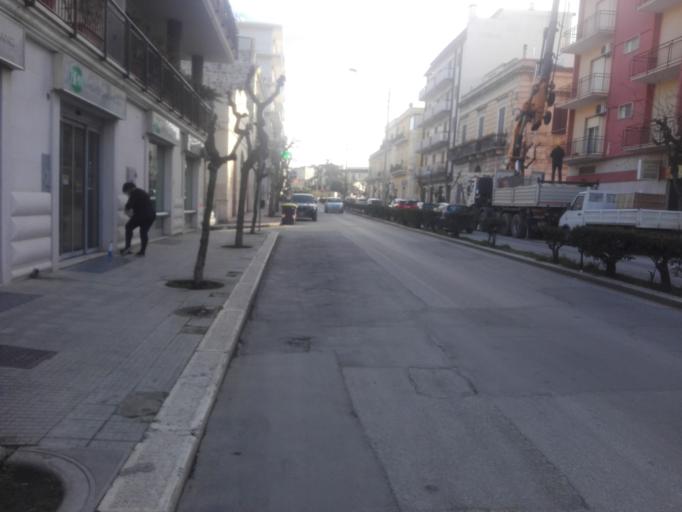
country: IT
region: Apulia
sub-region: Provincia di Bari
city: Corato
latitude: 41.1531
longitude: 16.4167
